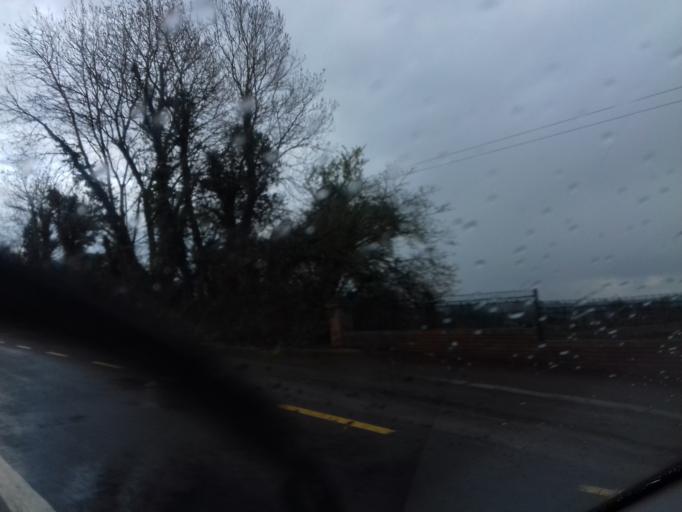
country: IE
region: Ulster
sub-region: An Cabhan
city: Ballyconnell
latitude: 54.1195
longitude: -7.6714
